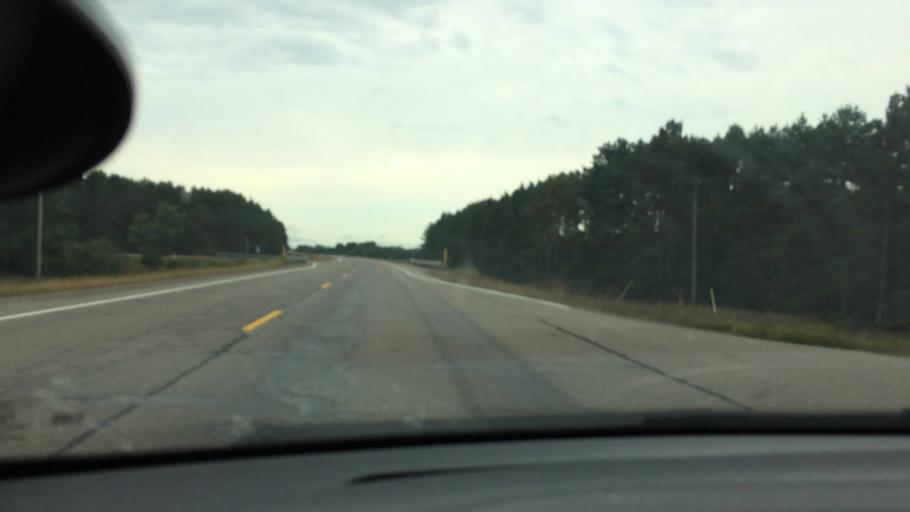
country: US
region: Wisconsin
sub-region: Eau Claire County
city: Augusta
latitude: 44.5834
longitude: -91.0934
